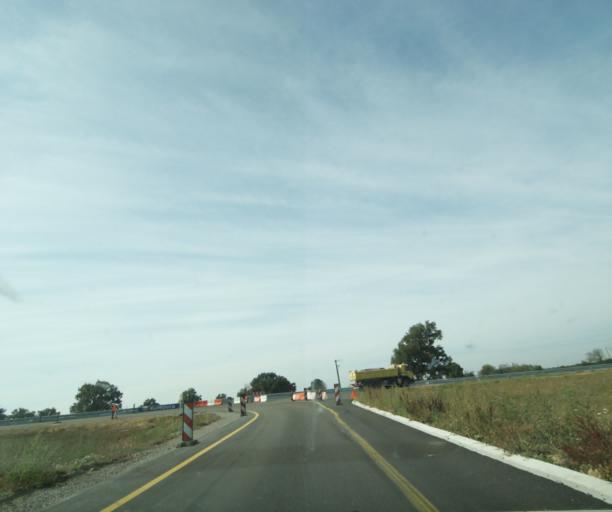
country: FR
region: Bourgogne
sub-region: Departement de Saone-et-Loire
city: Palinges
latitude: 46.5158
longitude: 4.1619
